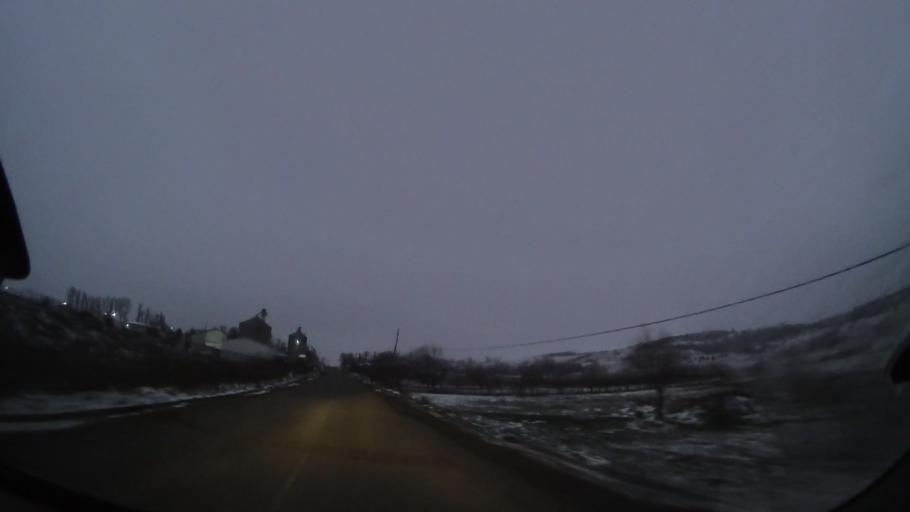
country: RO
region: Vaslui
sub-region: Comuna Dimitrie Cantemir
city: Dimitrie Cantemir
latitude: 46.4976
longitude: 28.0526
